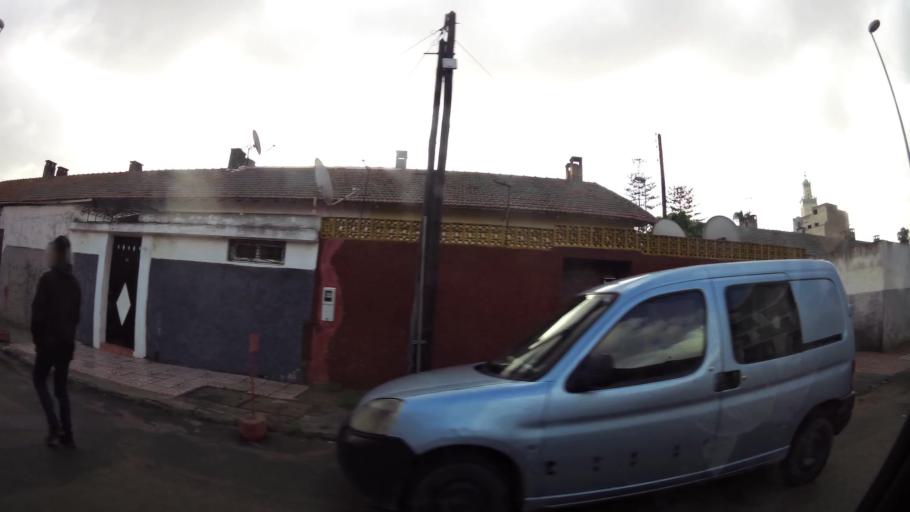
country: MA
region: Grand Casablanca
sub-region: Casablanca
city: Casablanca
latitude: 33.5636
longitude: -7.6470
